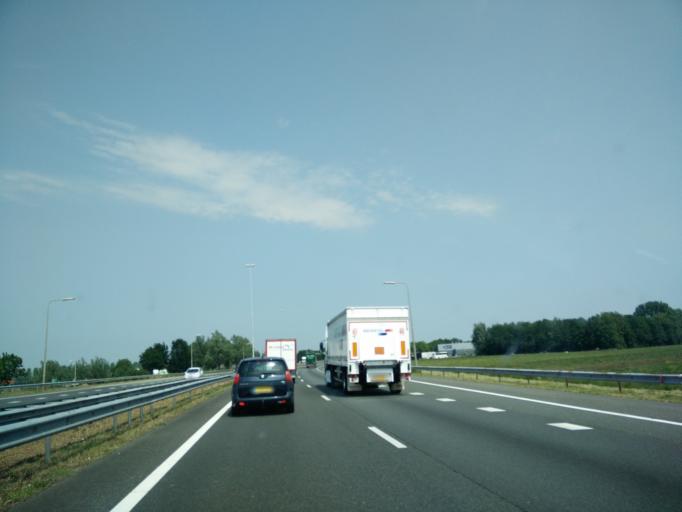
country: NL
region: Utrecht
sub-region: Gemeente IJsselstein
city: IJsselstein
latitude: 51.9521
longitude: 5.0183
